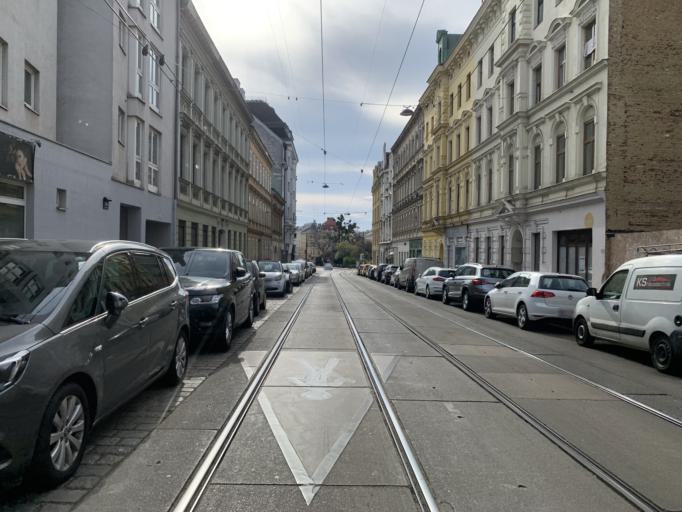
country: AT
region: Vienna
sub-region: Wien Stadt
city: Vienna
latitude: 48.2292
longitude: 16.3339
